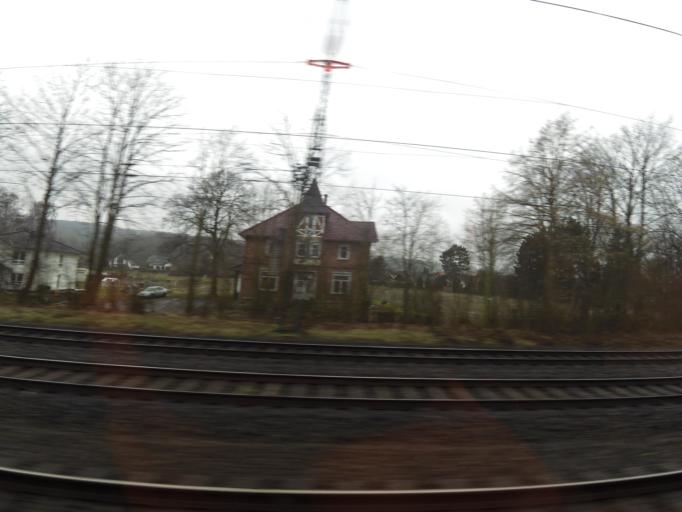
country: DE
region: North Rhine-Westphalia
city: Loehne
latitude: 52.1589
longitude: 8.6679
